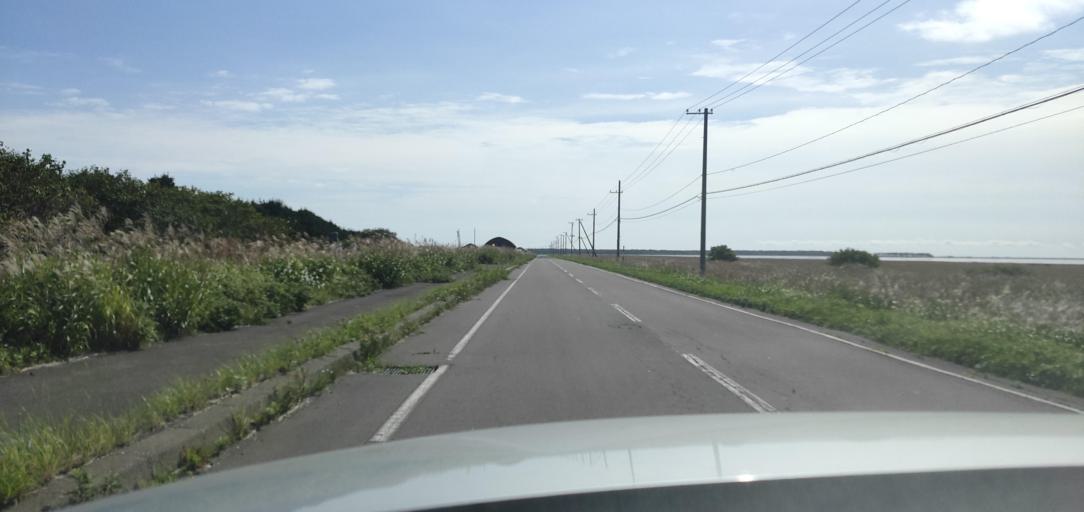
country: JP
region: Hokkaido
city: Shibetsu
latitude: 43.6188
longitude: 145.2313
